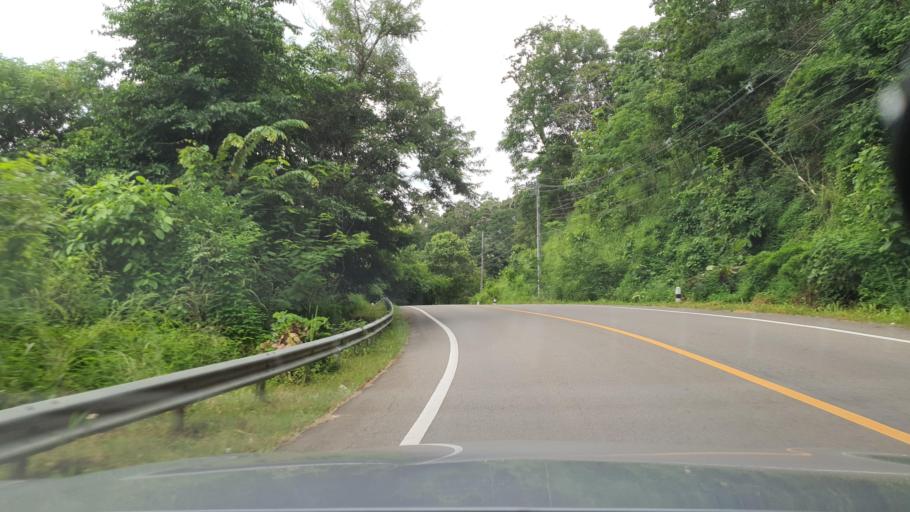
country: TH
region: Chiang Mai
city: Mae Wang
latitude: 18.6219
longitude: 98.7234
